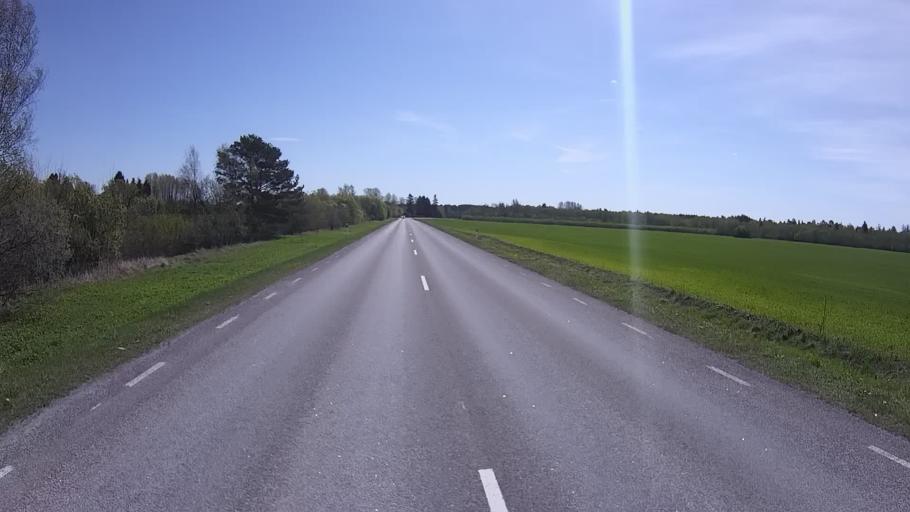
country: EE
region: Laeaene
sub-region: Ridala Parish
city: Uuemoisa
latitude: 58.8591
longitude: 23.6314
